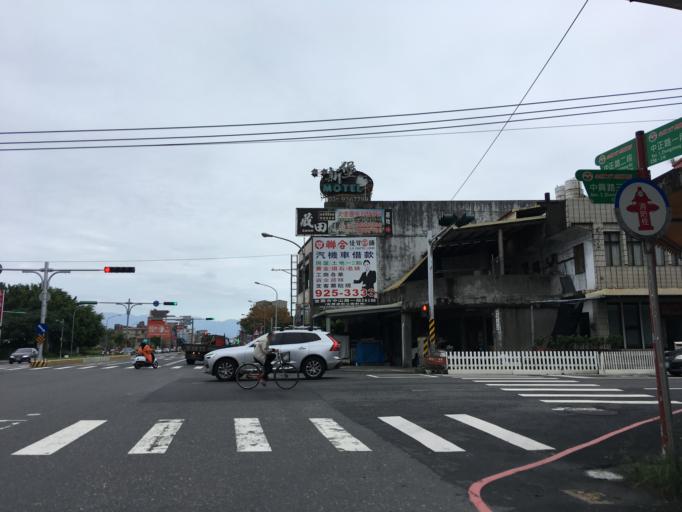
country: TW
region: Taiwan
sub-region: Yilan
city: Yilan
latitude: 24.6927
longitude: 121.7700
